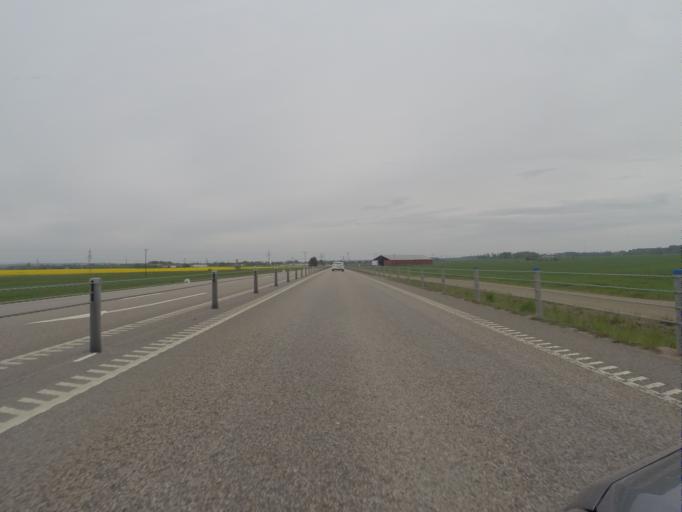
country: SE
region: Skane
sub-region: Helsingborg
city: Morarp
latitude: 56.0882
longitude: 12.8745
